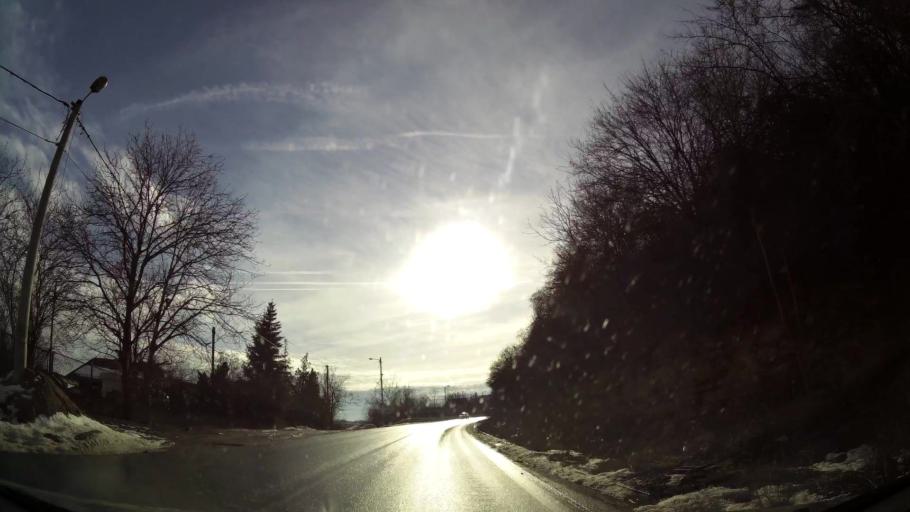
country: RS
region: Central Serbia
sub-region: Belgrade
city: Rakovica
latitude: 44.7188
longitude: 20.4311
